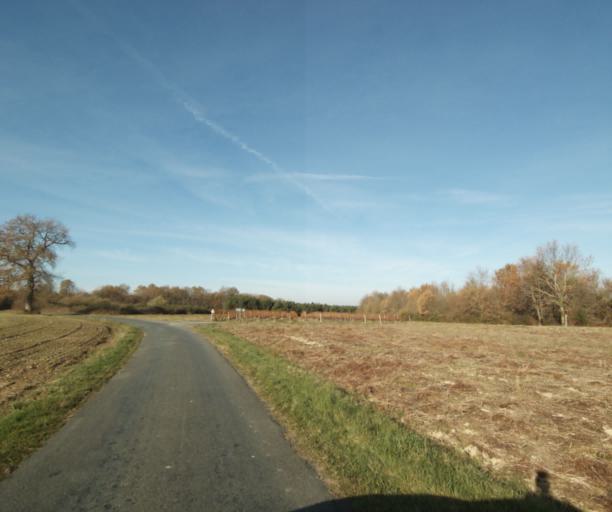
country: FR
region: Poitou-Charentes
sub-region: Departement de la Charente-Maritime
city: Cherac
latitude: 45.7449
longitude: -0.4713
